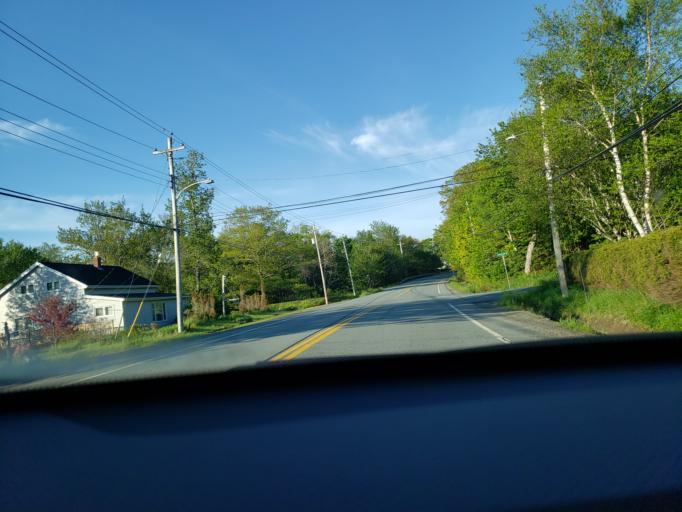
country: CA
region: Nova Scotia
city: Cole Harbour
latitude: 44.7362
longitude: -63.3885
